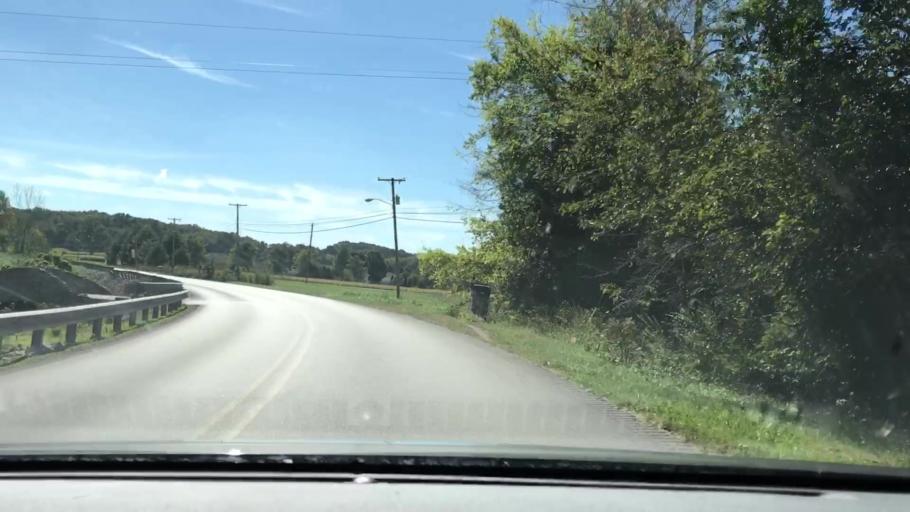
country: US
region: Kentucky
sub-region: Logan County
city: Russellville
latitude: 36.8361
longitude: -86.8707
